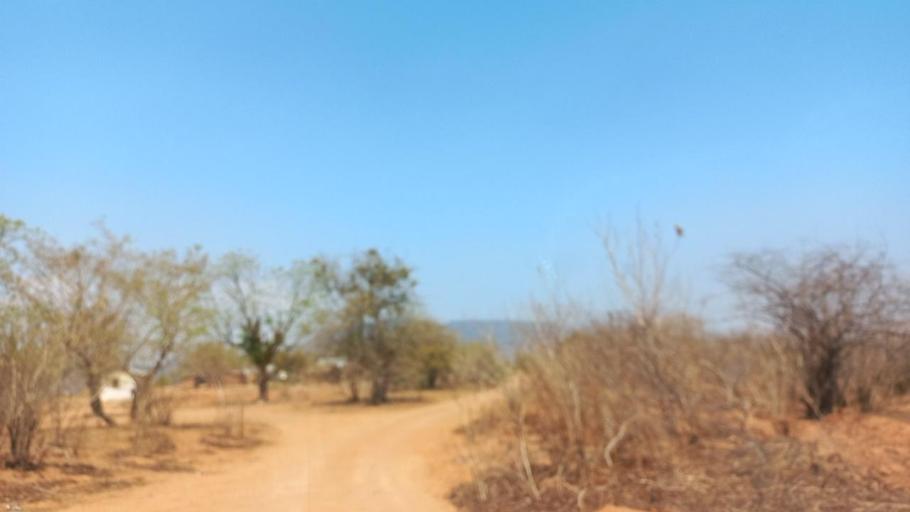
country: ZM
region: Lusaka
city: Luangwa
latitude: -15.5908
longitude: 30.3885
